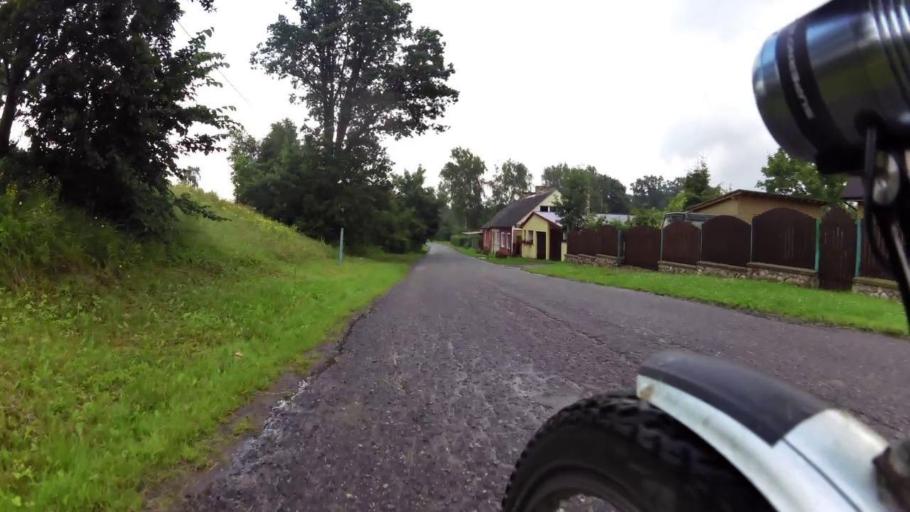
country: PL
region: West Pomeranian Voivodeship
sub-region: Powiat lobeski
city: Lobez
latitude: 53.7297
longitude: 15.6401
